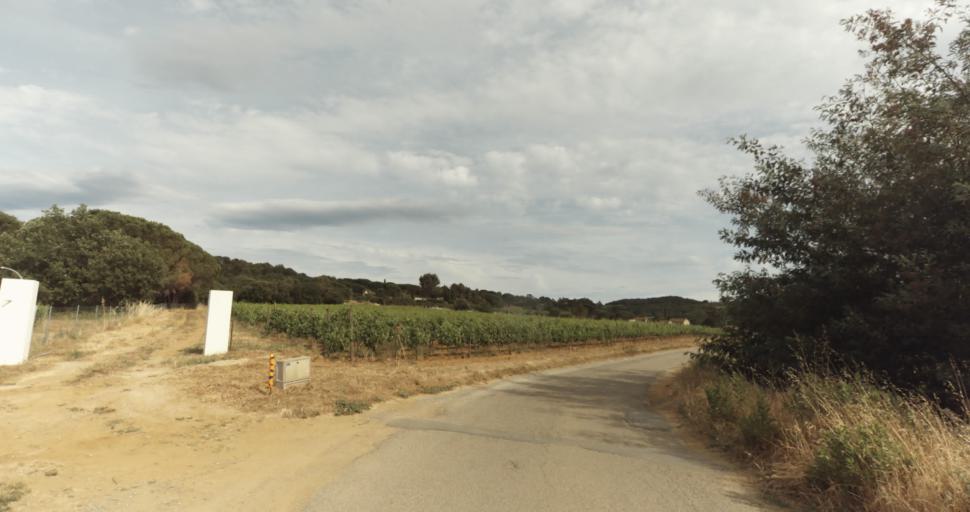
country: FR
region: Provence-Alpes-Cote d'Azur
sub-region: Departement du Var
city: Gassin
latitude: 43.2172
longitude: 6.5800
